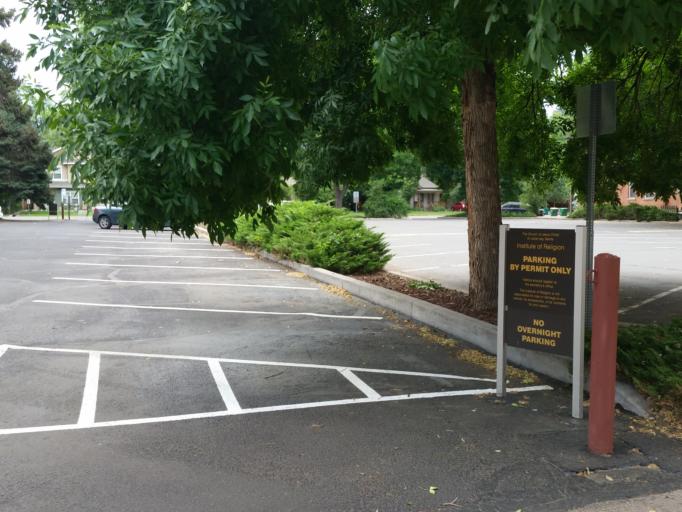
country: US
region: Colorado
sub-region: Larimer County
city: Fort Collins
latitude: 40.5793
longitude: -105.0816
